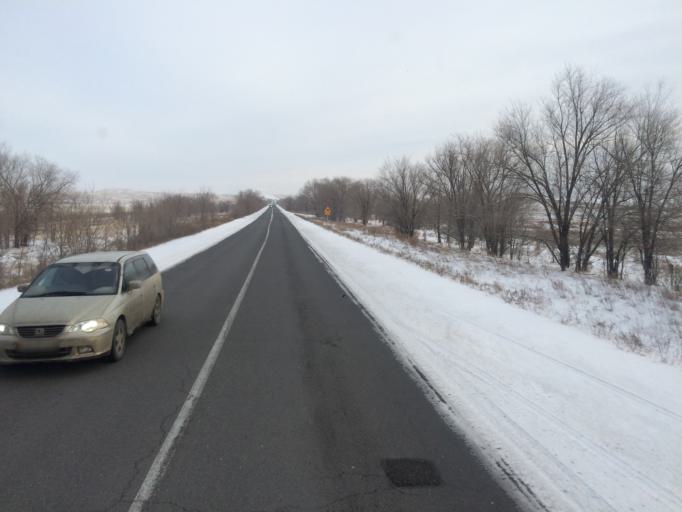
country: KG
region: Chuy
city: Bystrovka
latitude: 43.3280
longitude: 75.9001
